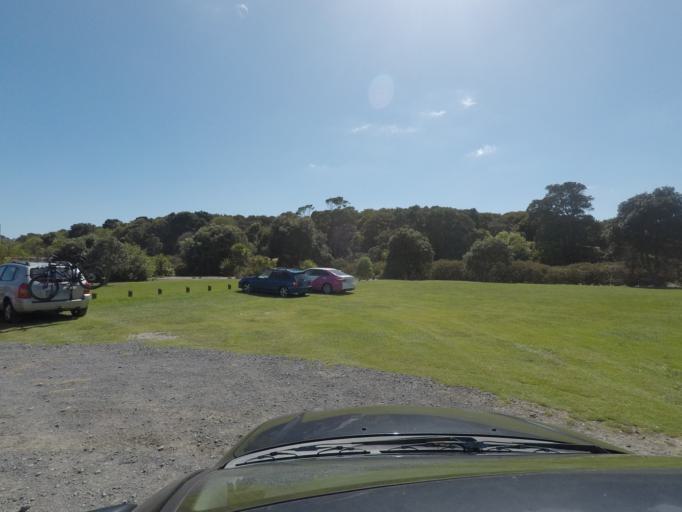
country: NZ
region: Auckland
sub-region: Auckland
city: Pakuranga
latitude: -36.8825
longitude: 175.0185
